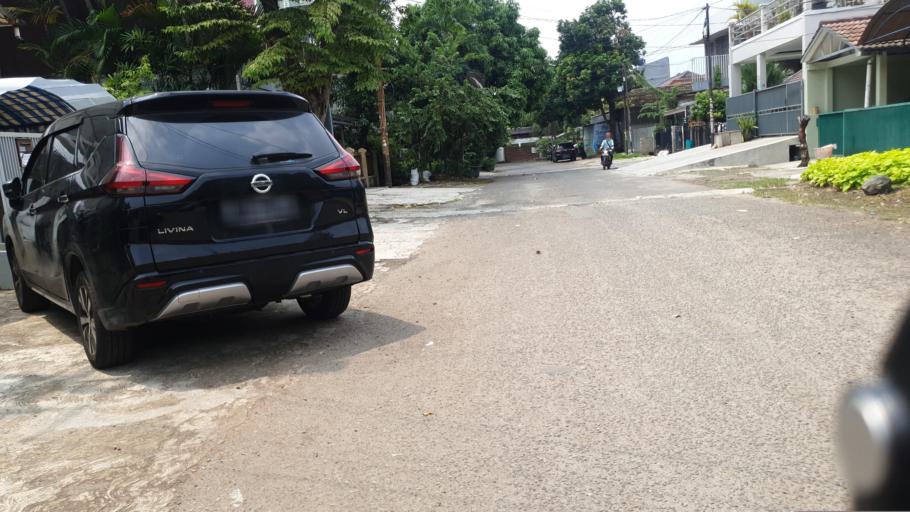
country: ID
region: West Java
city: Ciputat
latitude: -6.1946
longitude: 106.7549
